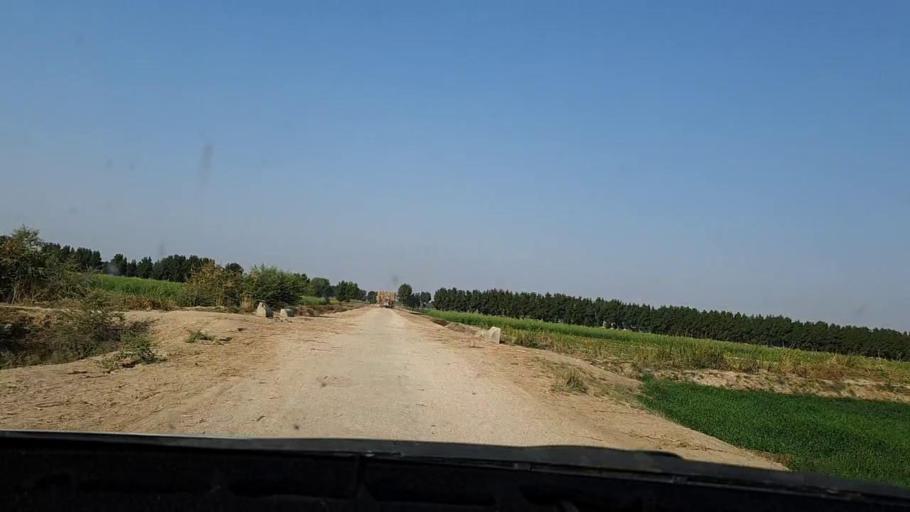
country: PK
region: Sindh
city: Tando Mittha Khan
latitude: 25.8236
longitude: 69.3063
